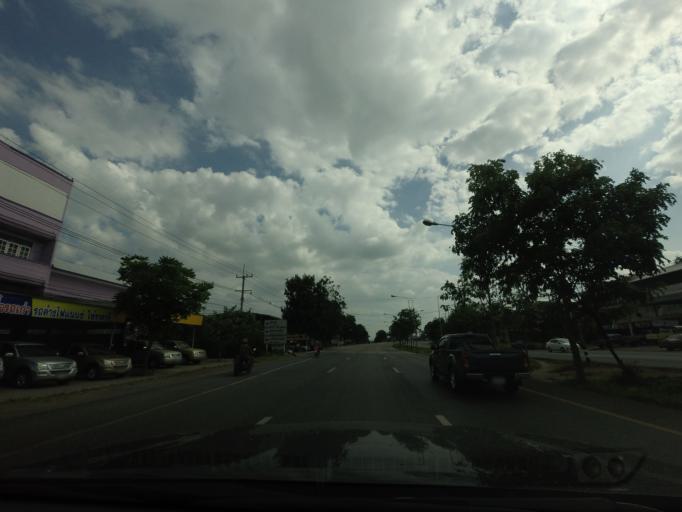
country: TH
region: Lop Buri
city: Chai Badan
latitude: 15.2204
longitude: 101.1276
